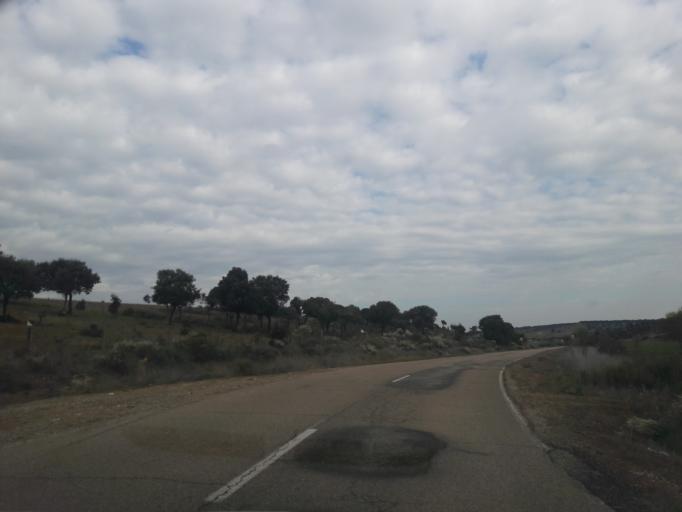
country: ES
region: Castille and Leon
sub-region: Provincia de Salamanca
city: Pastores
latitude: 40.5333
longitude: -6.5258
